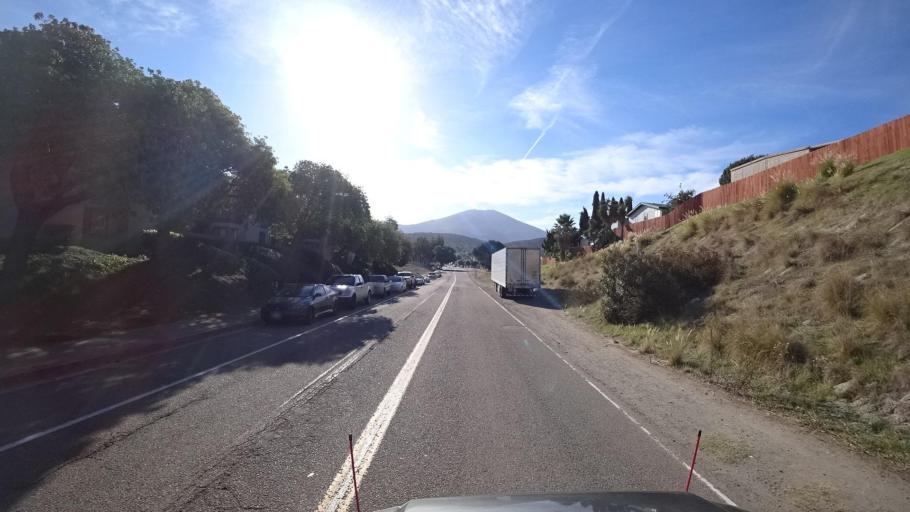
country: US
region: California
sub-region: San Diego County
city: Rancho San Diego
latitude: 32.7323
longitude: -116.9620
